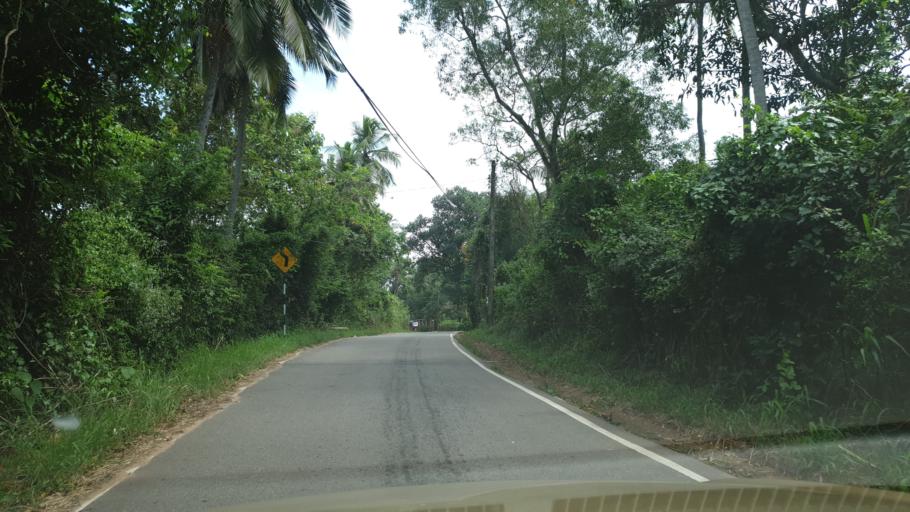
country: LK
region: North Western
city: Kuliyapitiya
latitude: 7.3543
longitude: 79.9714
